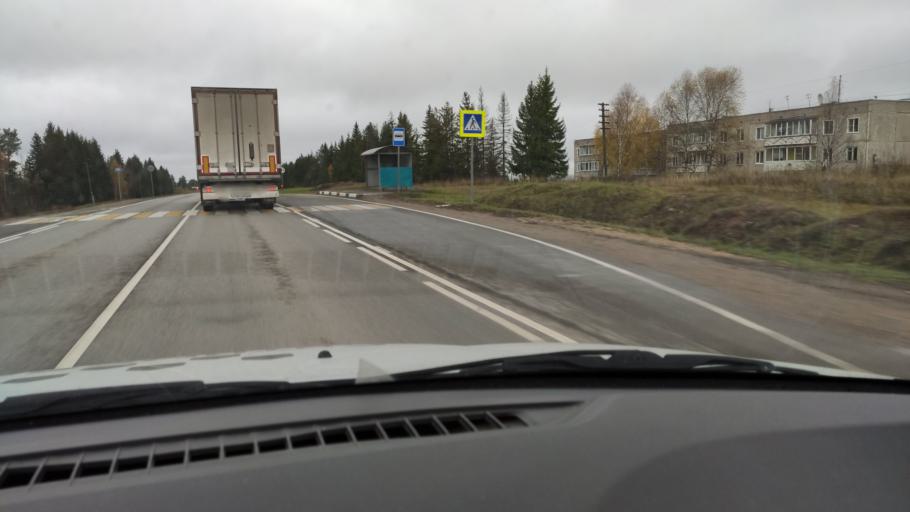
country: RU
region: Kirov
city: Slobodskoy
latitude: 58.7464
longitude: 50.3070
